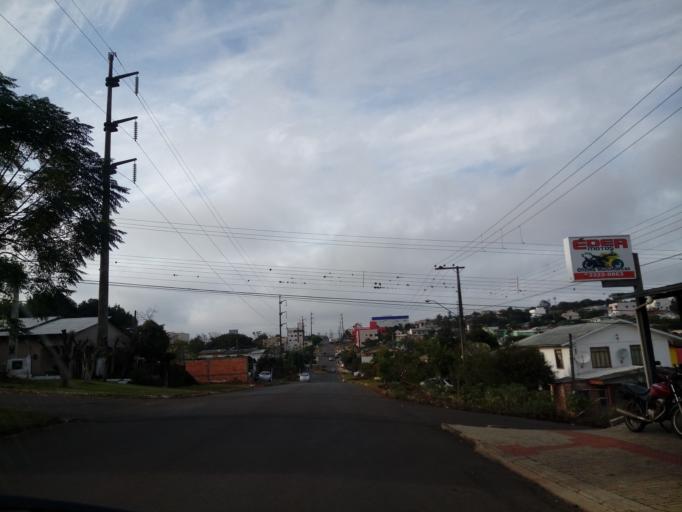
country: BR
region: Santa Catarina
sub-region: Chapeco
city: Chapeco
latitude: -27.0793
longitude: -52.6352
